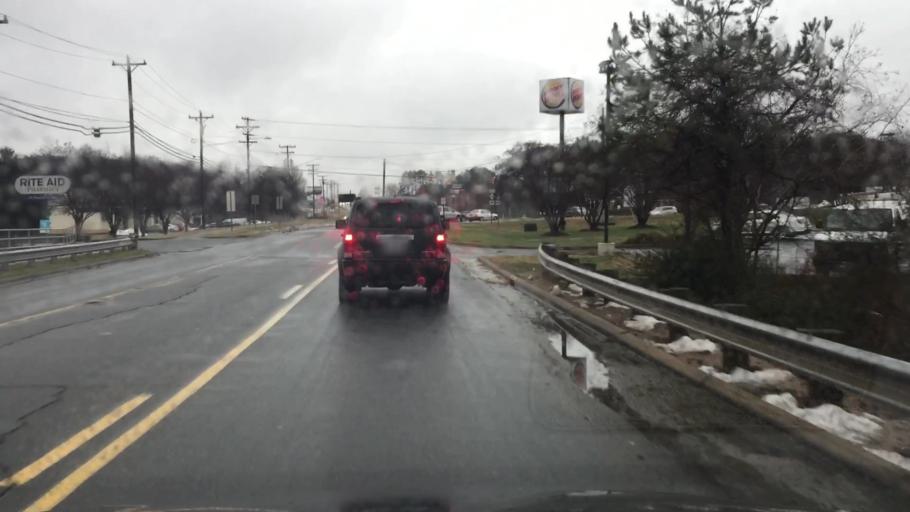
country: US
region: North Carolina
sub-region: Iredell County
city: Mooresville
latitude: 35.5878
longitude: -80.8269
